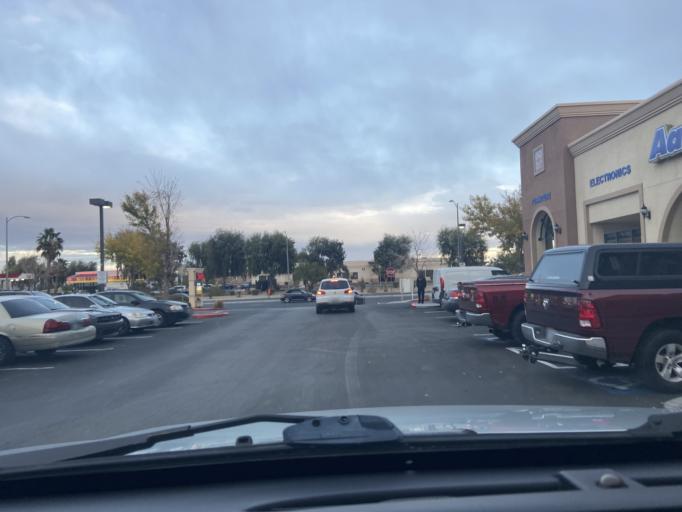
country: US
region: Nevada
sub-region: Clark County
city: North Las Vegas
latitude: 36.2384
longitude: -115.1809
